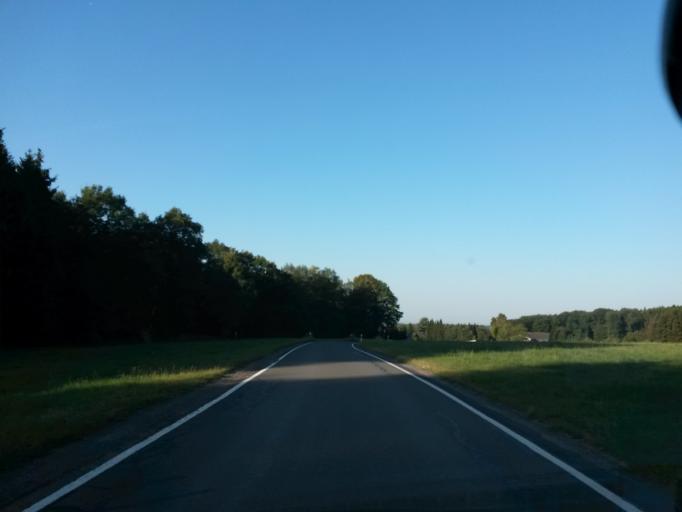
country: DE
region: North Rhine-Westphalia
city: Wipperfurth
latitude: 51.0918
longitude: 7.4100
